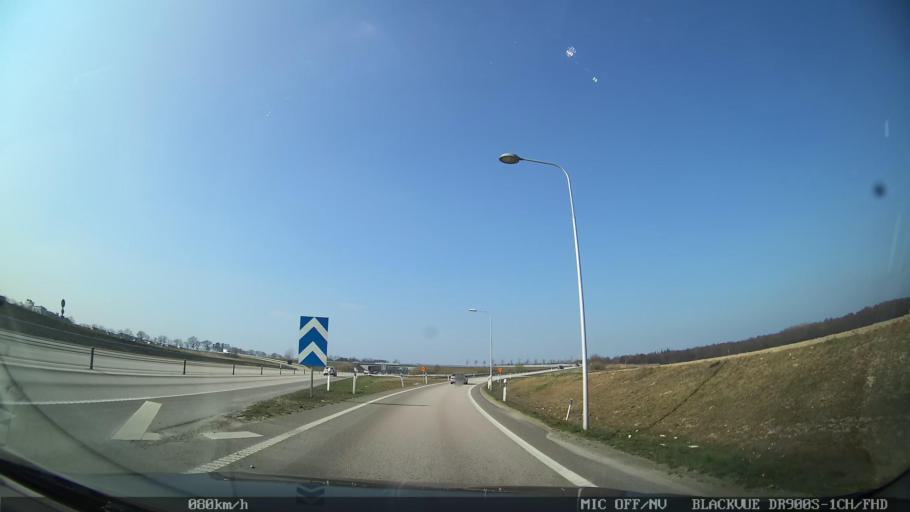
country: SE
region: Skane
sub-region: Helsingborg
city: Odakra
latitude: 56.0815
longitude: 12.7173
